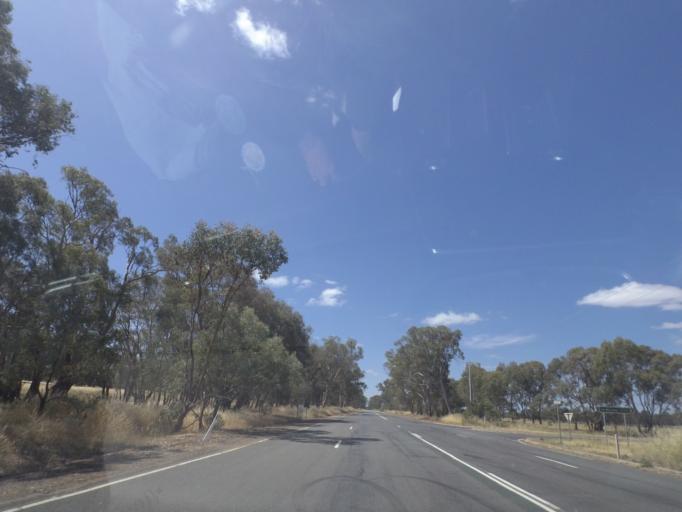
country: AU
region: Victoria
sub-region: Wangaratta
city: Wangaratta
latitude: -36.4262
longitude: 146.2571
